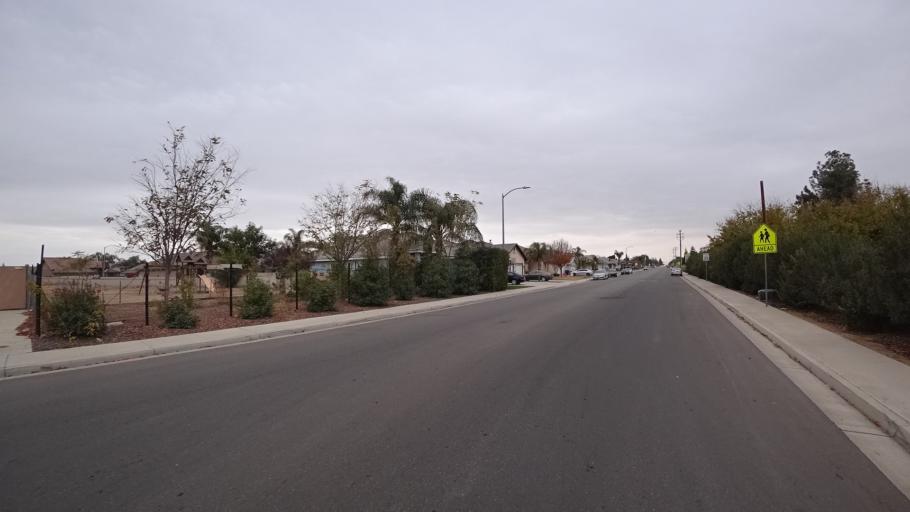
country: US
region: California
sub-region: Kern County
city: Greenfield
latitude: 35.2887
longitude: -119.0323
